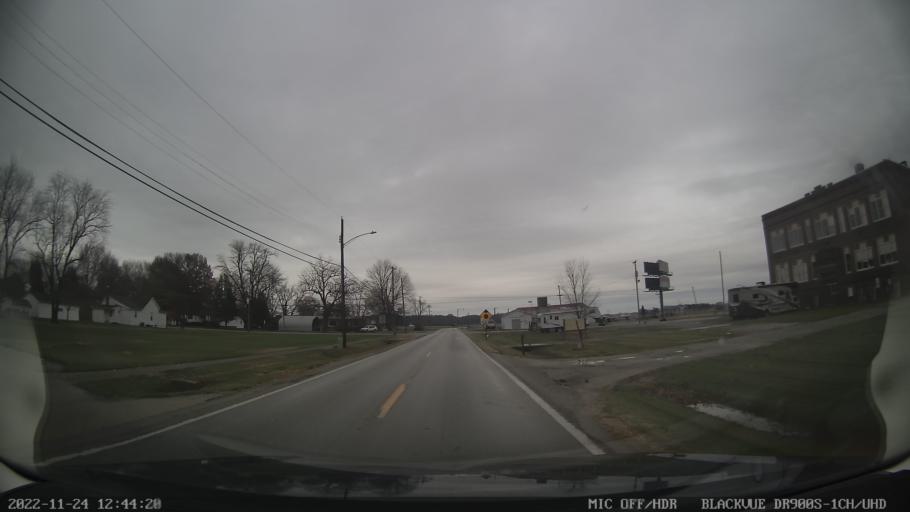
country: US
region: Illinois
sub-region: Macoupin County
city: Staunton
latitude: 38.9613
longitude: -89.7653
